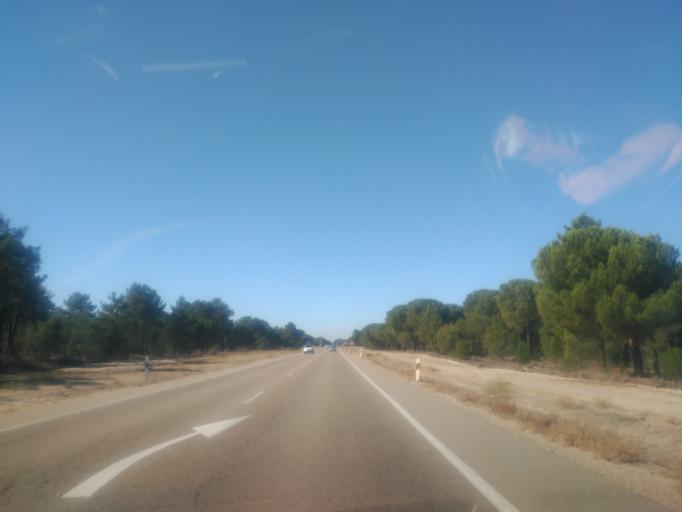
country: ES
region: Castille and Leon
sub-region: Provincia de Valladolid
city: Traspinedo
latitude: 41.6008
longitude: -4.4805
